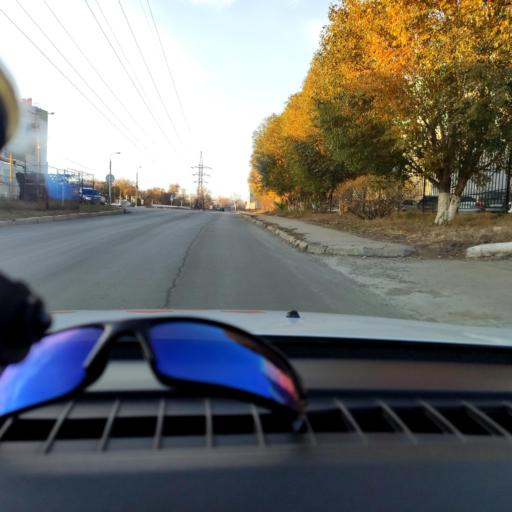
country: RU
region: Samara
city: Samara
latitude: 53.1830
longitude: 50.1740
